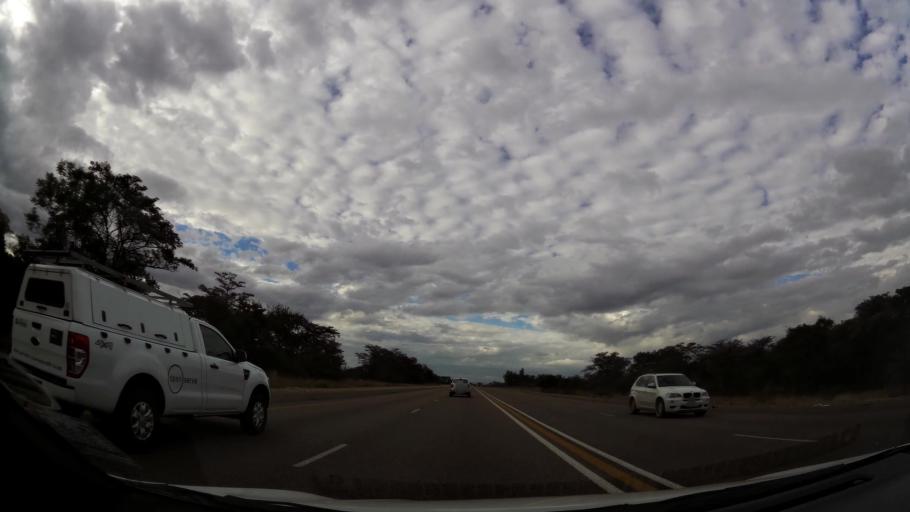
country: ZA
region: Limpopo
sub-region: Waterberg District Municipality
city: Modimolle
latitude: -24.5853
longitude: 28.6677
